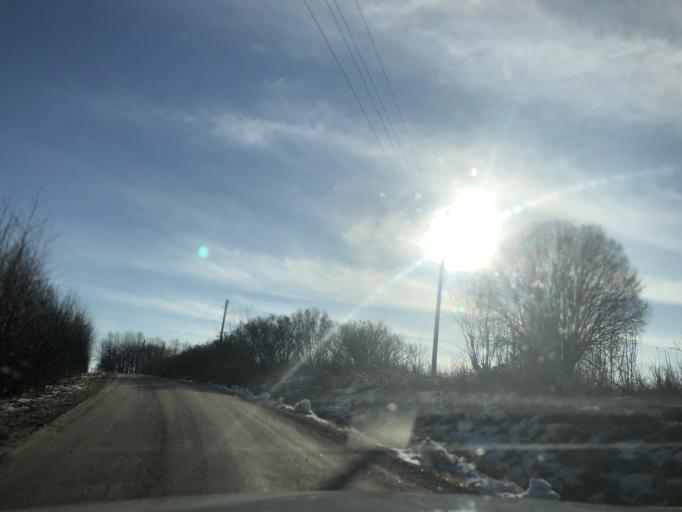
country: SE
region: Vaestra Goetaland
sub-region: Ulricehamns Kommun
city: Ulricehamn
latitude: 57.7965
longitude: 13.4474
